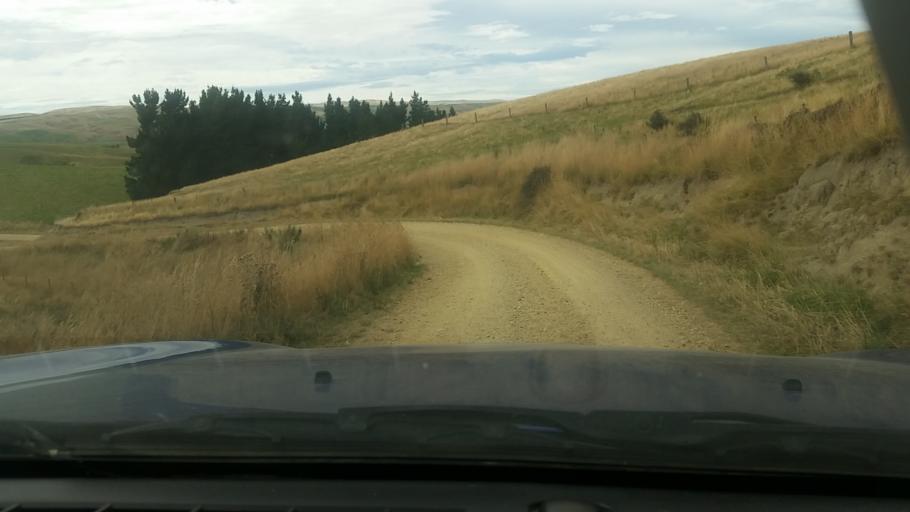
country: NZ
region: Southland
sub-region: Gore District
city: Gore
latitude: -45.5839
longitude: 169.4137
